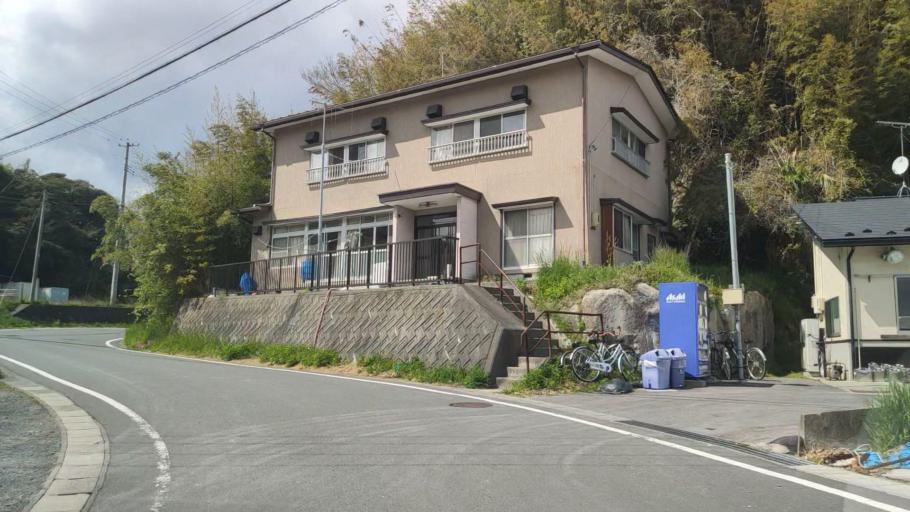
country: JP
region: Miyagi
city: Yamoto
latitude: 38.3354
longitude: 141.1650
